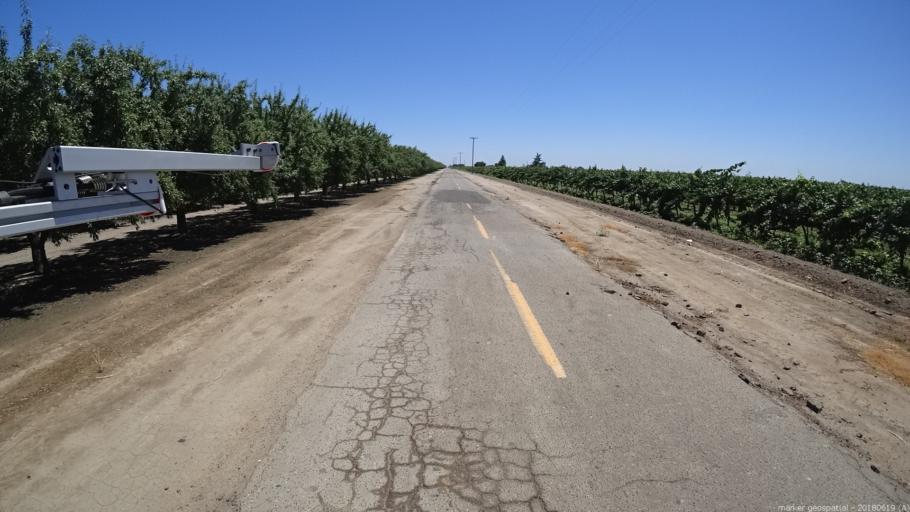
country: US
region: California
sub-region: Madera County
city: Parkwood
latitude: 36.8730
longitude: -120.1091
